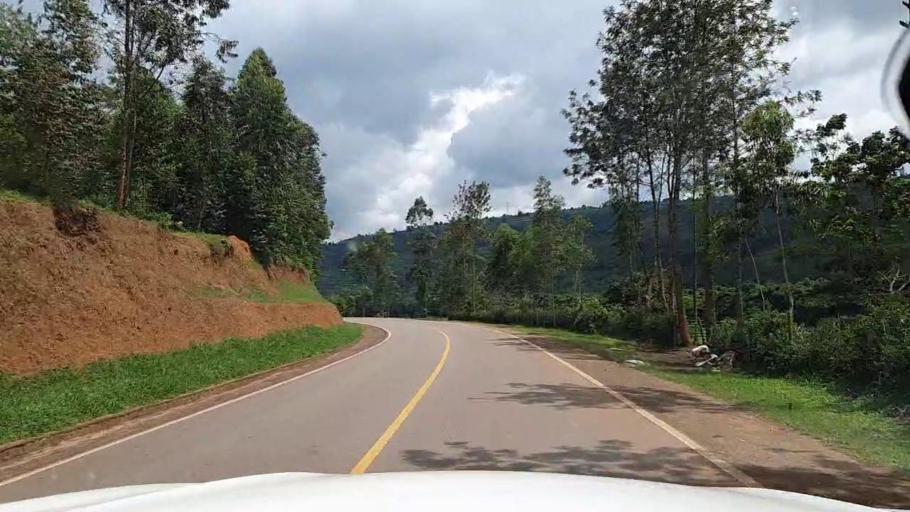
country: RW
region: Kigali
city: Kigali
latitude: -1.8029
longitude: 30.1276
